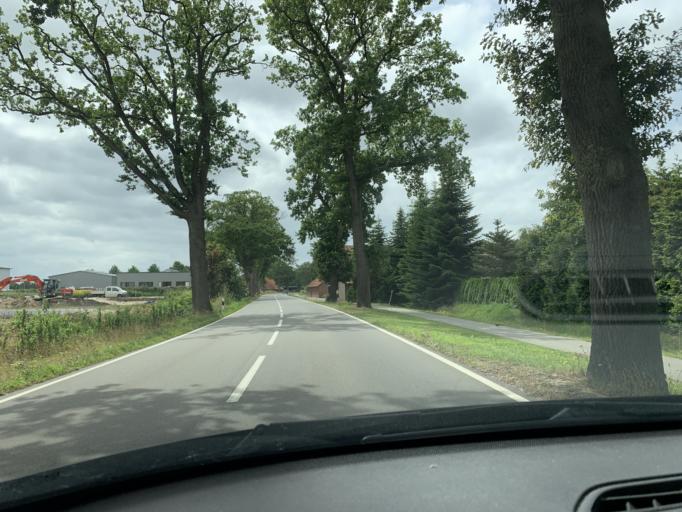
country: DE
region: Lower Saxony
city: Westerstede
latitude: 53.2735
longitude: 7.9526
